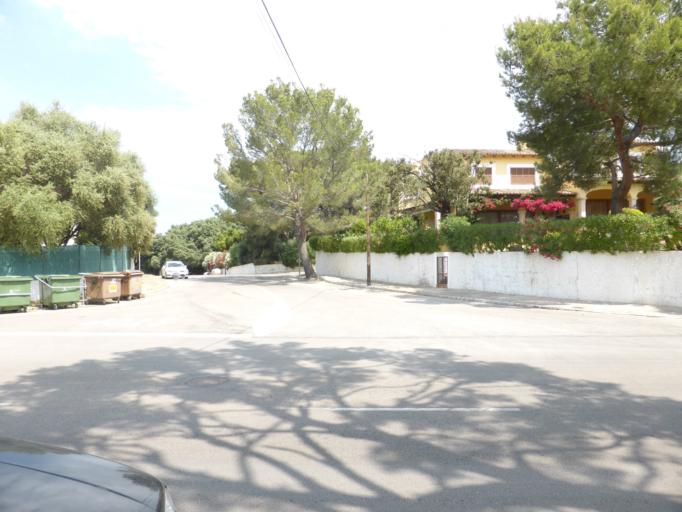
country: ES
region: Balearic Islands
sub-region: Illes Balears
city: Port d'Alcudia
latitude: 39.8363
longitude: 3.1482
